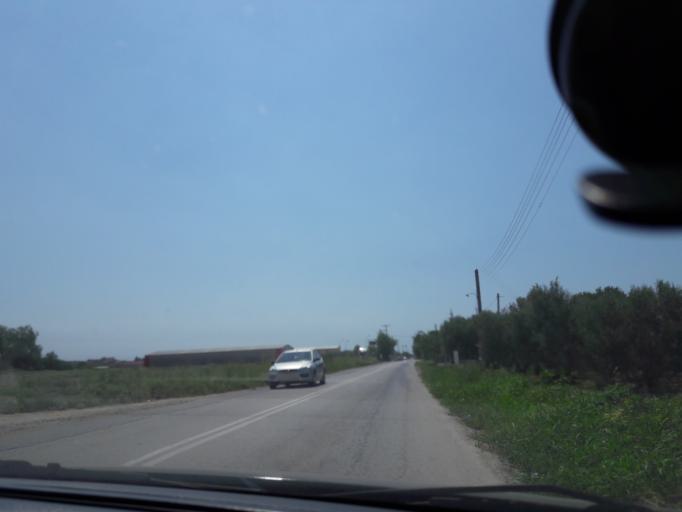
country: GR
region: Central Macedonia
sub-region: Nomos Chalkidikis
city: Nea Kallikrateia
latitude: 40.3373
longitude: 23.0645
